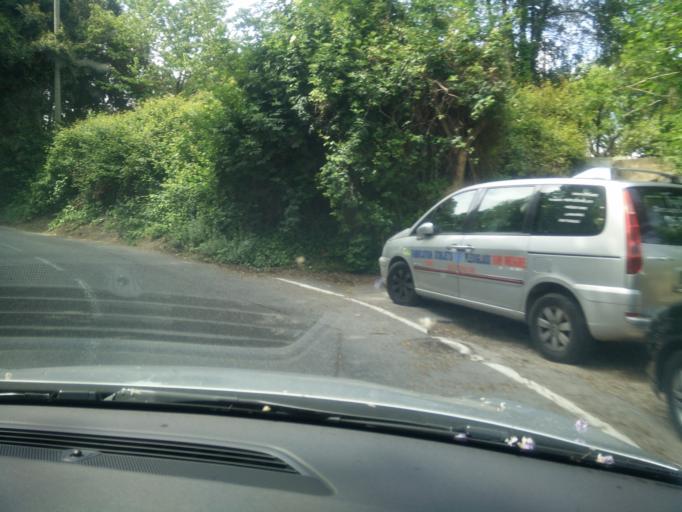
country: FR
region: Provence-Alpes-Cote d'Azur
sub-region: Departement des Alpes-Maritimes
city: Biot
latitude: 43.5949
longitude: 7.1042
